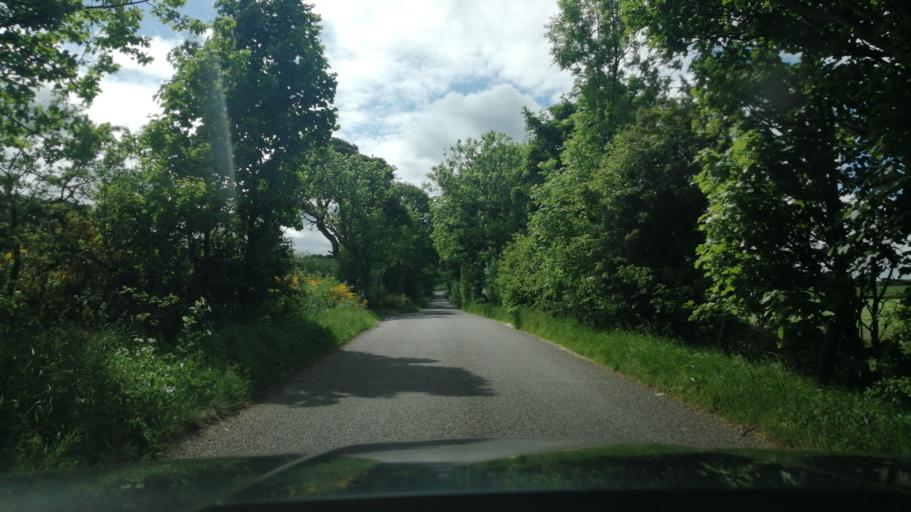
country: GB
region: Scotland
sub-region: Moray
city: Elgin
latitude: 57.6542
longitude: -3.2708
